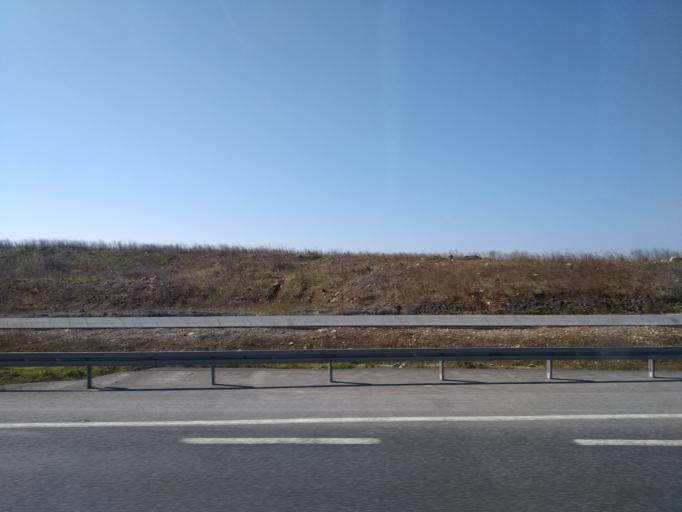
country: TR
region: Istanbul
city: Mahmut Sevket Pasa
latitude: 41.1268
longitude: 29.2861
